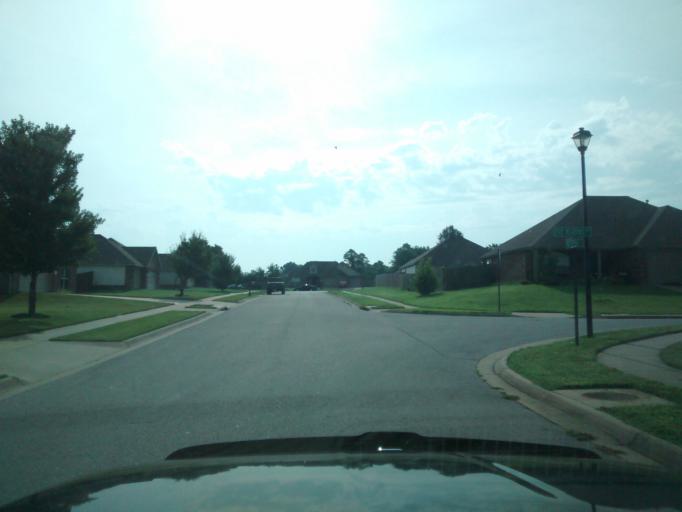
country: US
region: Arkansas
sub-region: Washington County
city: Farmington
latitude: 36.0746
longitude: -94.2841
